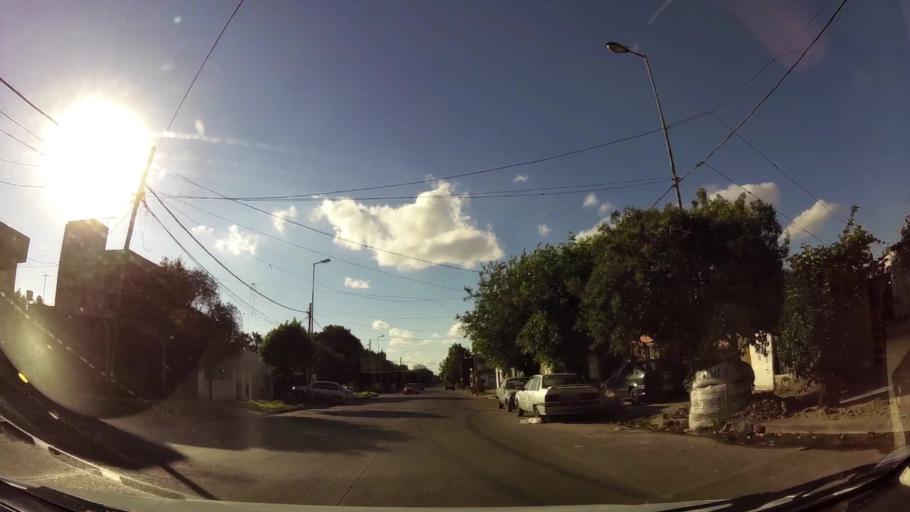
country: AR
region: Buenos Aires
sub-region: Partido de Moron
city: Moron
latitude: -34.6791
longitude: -58.6176
